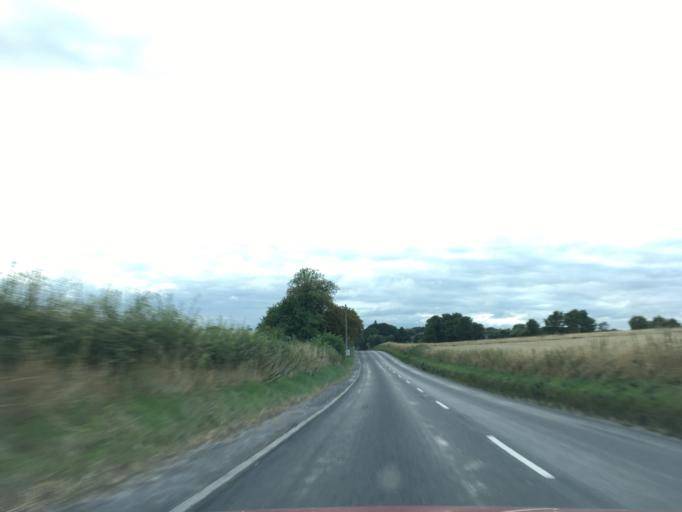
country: GB
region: England
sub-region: Wiltshire
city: Devizes
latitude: 51.3384
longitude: -1.9625
